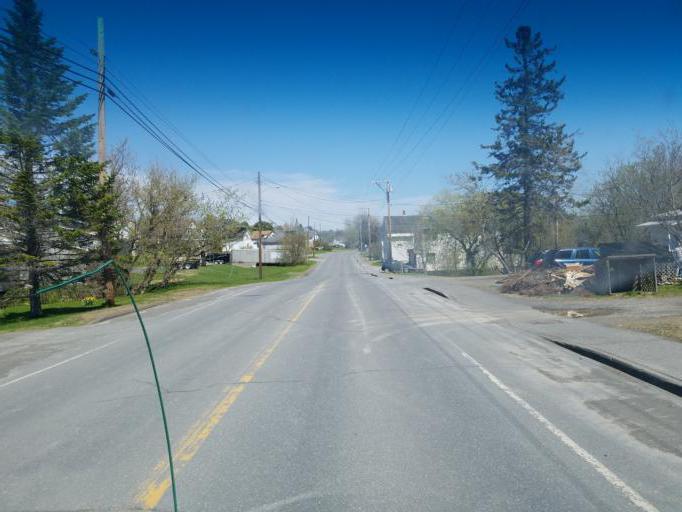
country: US
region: Maine
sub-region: Aroostook County
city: Caribou
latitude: 46.8576
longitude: -68.0217
